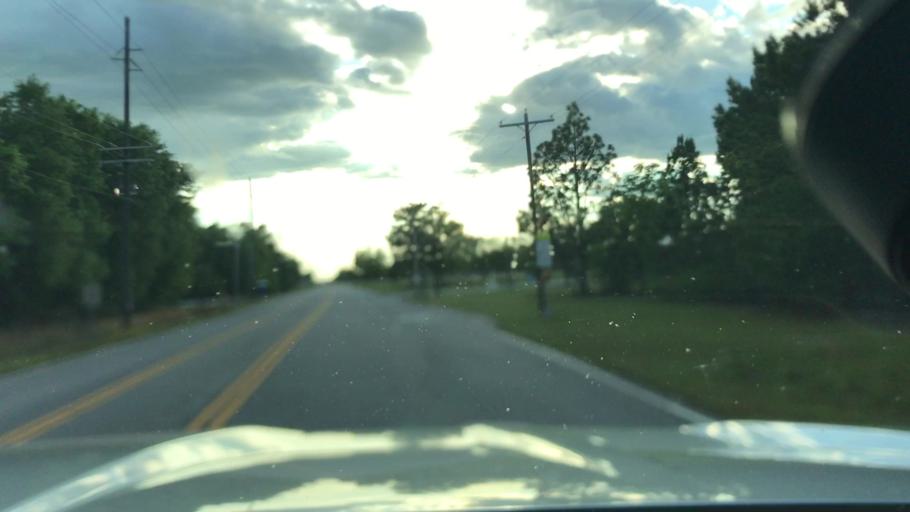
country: US
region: South Carolina
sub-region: Barnwell County
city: Blackville
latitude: 33.4741
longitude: -81.1847
